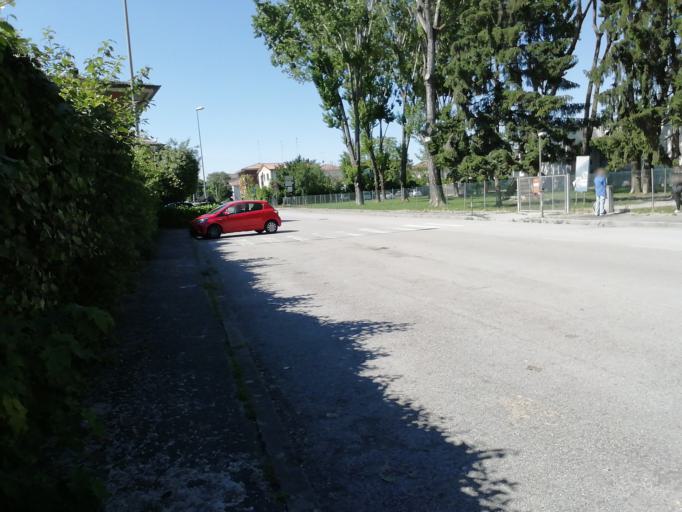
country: IT
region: Veneto
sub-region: Provincia di Padova
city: Cadoneghe
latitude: 45.4167
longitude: 11.9162
